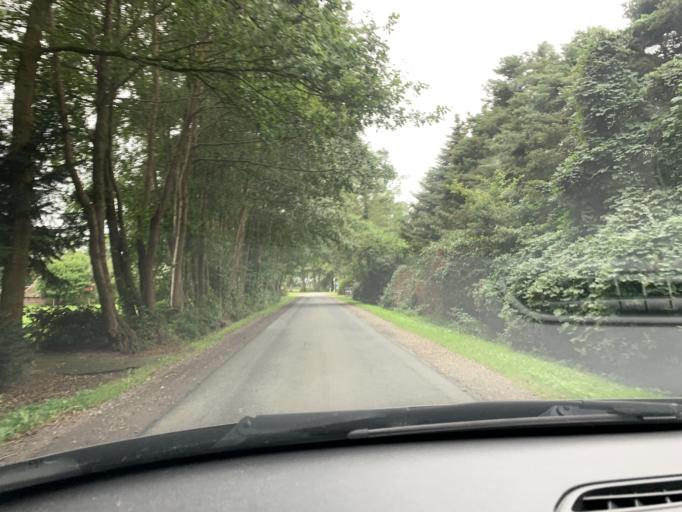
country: DE
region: Lower Saxony
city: Westerstede
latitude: 53.2787
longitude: 7.8878
